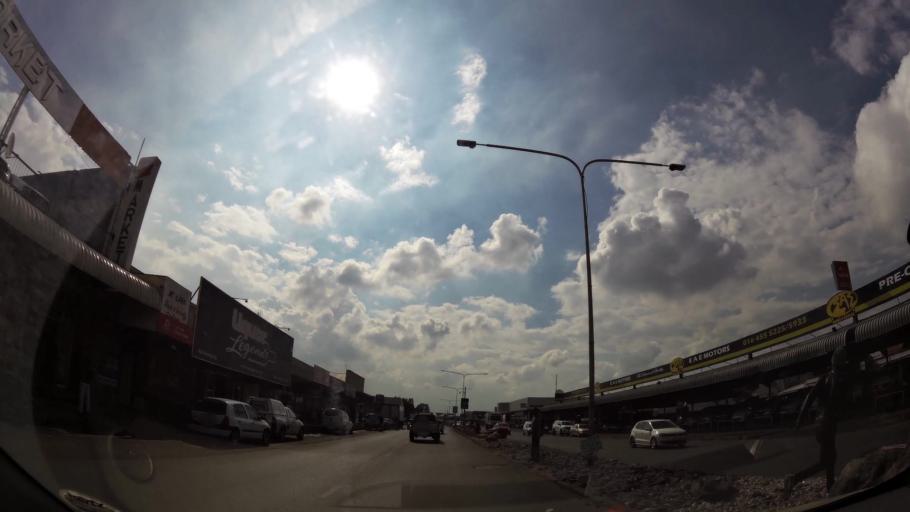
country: ZA
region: Gauteng
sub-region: Sedibeng District Municipality
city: Vereeniging
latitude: -26.6707
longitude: 27.9325
